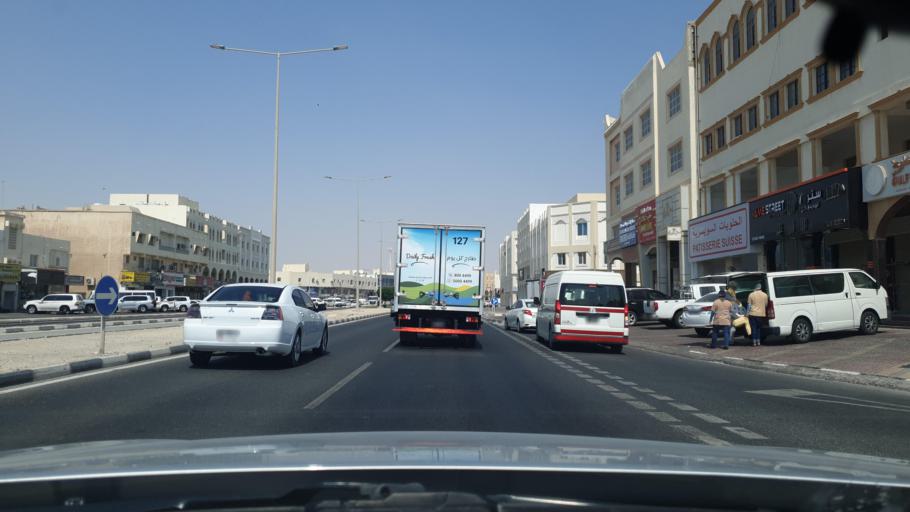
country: QA
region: Al Khawr
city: Al Khawr
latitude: 25.6836
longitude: 51.4959
